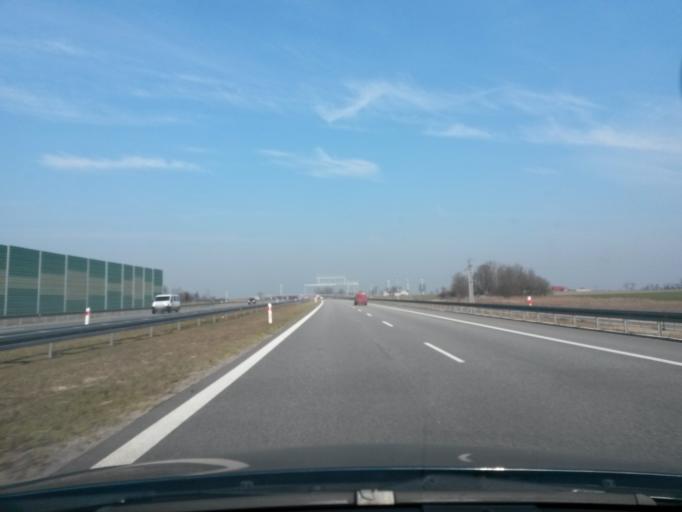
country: PL
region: Lodz Voivodeship
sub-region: Powiat kutnowski
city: Krzyzanow
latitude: 52.2049
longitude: 19.4838
